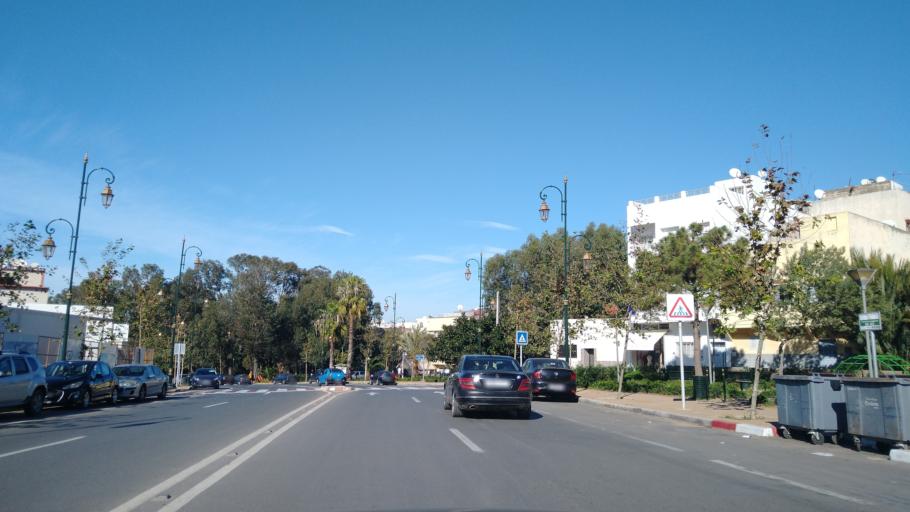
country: MA
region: Rabat-Sale-Zemmour-Zaer
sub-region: Rabat
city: Rabat
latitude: 33.9969
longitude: -6.8190
